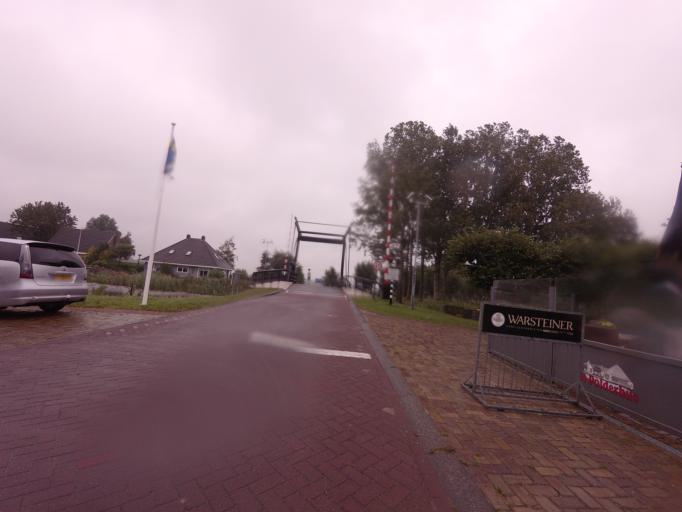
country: NL
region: Friesland
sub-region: Gemeente Smallingerland
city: Oudega
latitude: 53.0969
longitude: 5.9516
